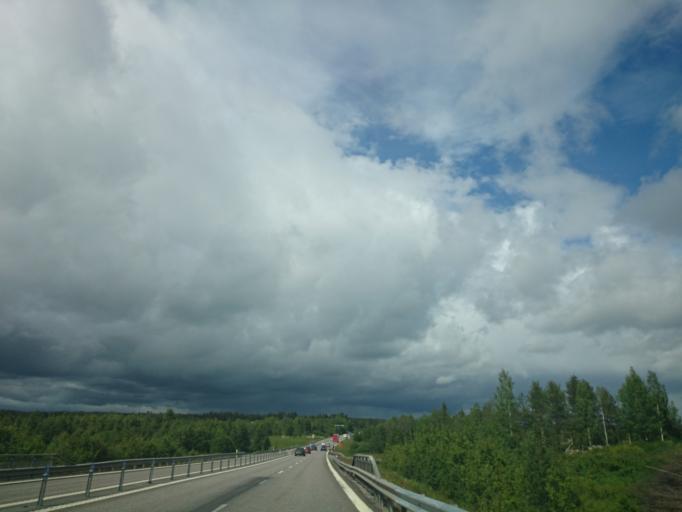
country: SE
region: Vaesternorrland
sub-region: Sundsvalls Kommun
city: Njurundabommen
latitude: 62.2220
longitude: 17.3718
